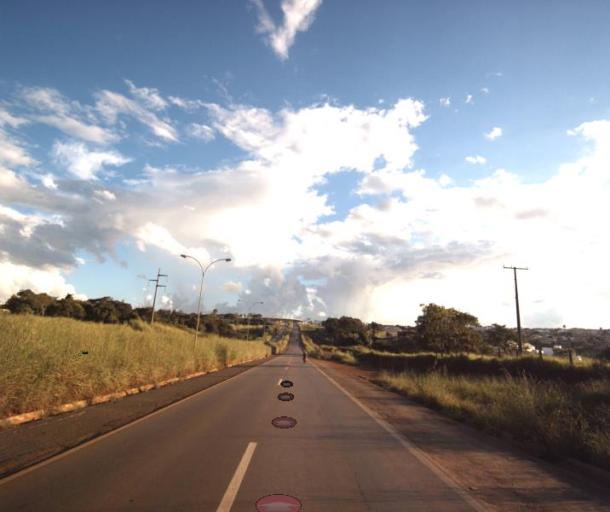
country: BR
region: Goias
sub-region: Anapolis
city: Anapolis
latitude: -16.3456
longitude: -48.9256
